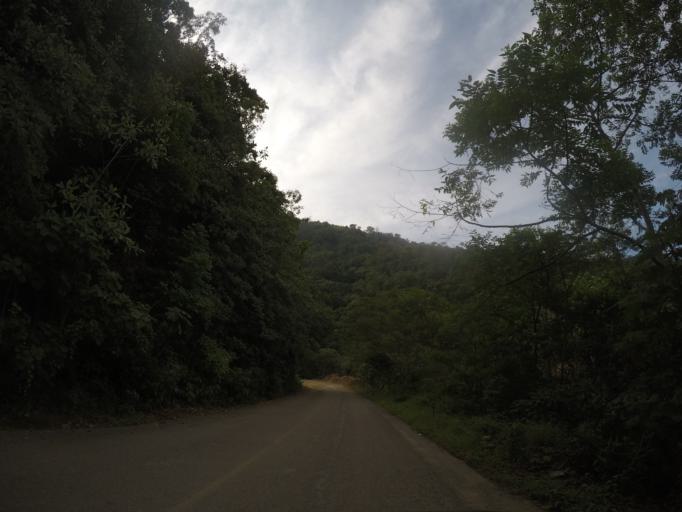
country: MX
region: Oaxaca
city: Pluma Hidalgo
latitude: 15.9477
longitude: -96.4395
